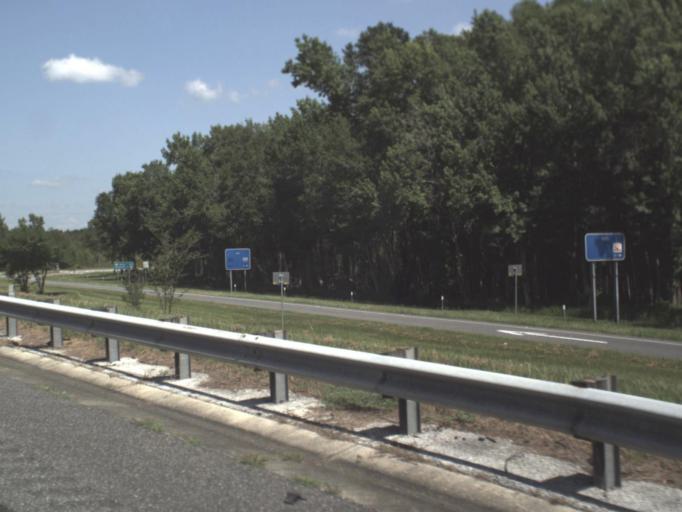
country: US
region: Florida
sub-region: Madison County
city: Madison
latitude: 30.4334
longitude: -83.6243
